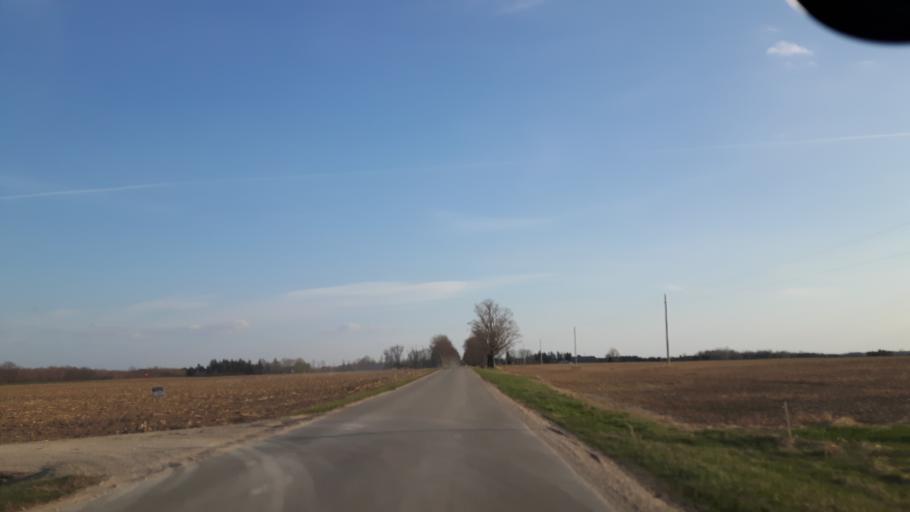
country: CA
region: Ontario
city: Goderich
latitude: 43.6318
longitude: -81.6643
